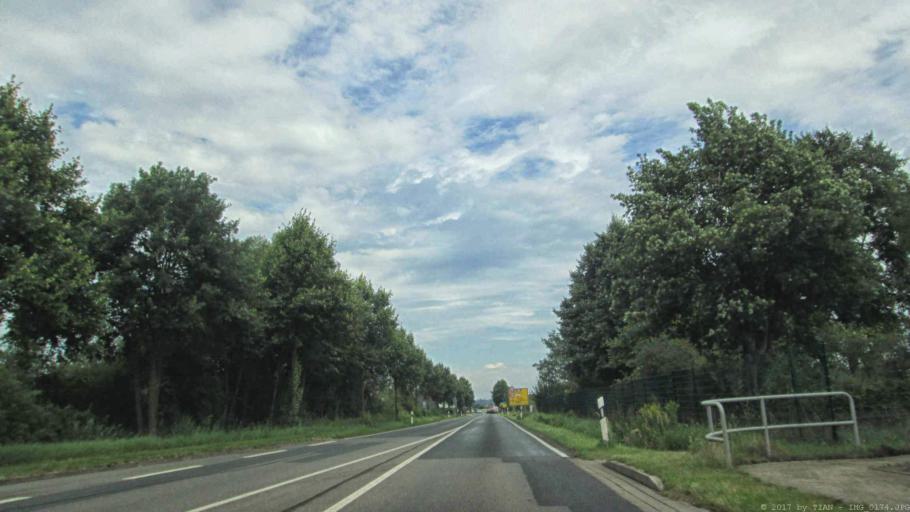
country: DE
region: Lower Saxony
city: Danndorf
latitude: 52.4160
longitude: 10.8480
